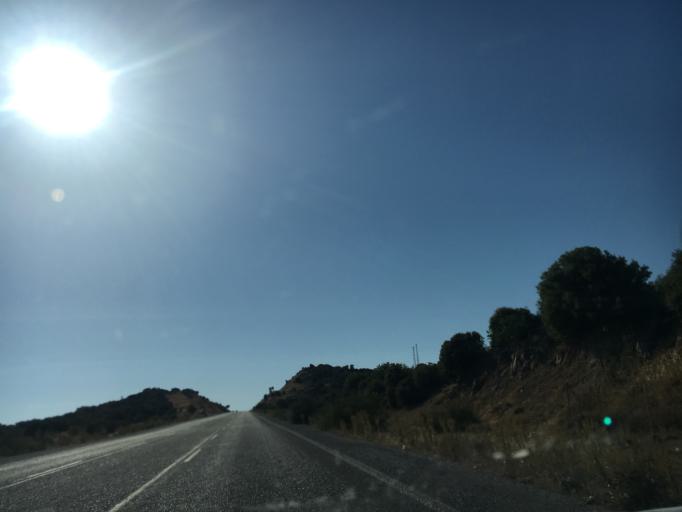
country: TR
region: Canakkale
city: Behram
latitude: 39.5062
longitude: 26.3946
